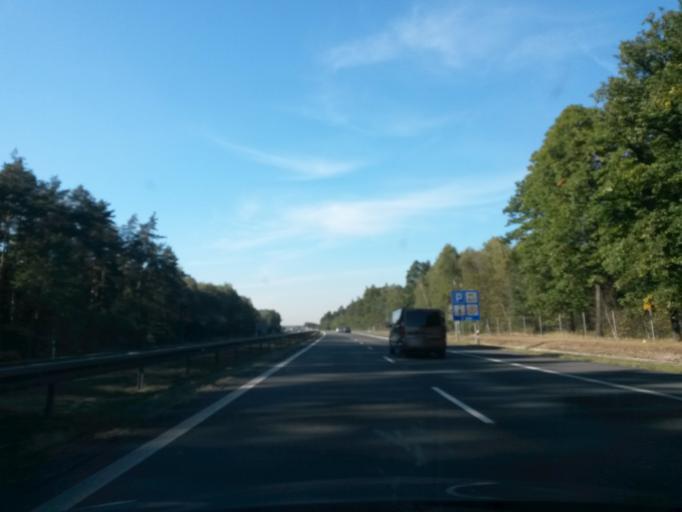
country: PL
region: Opole Voivodeship
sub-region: Powiat opolski
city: Proszkow
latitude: 50.5539
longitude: 17.8866
